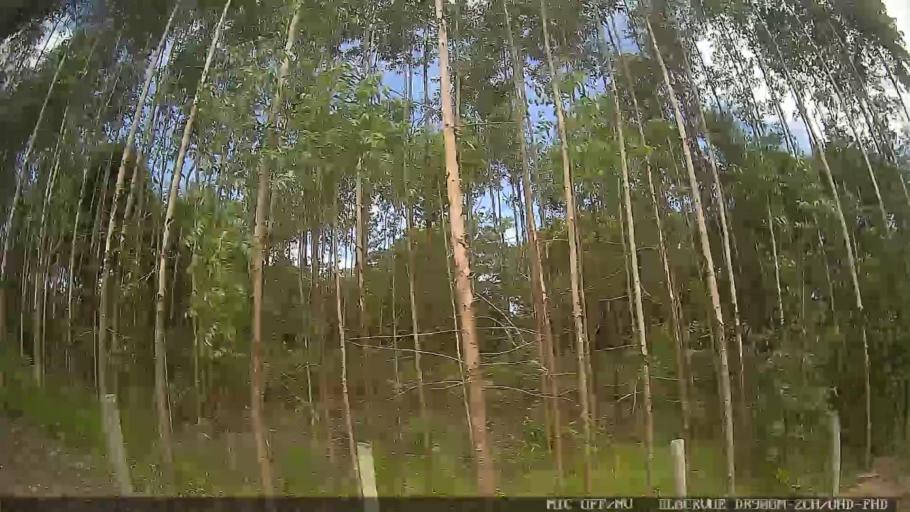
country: BR
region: Sao Paulo
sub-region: Conchas
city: Conchas
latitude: -22.9988
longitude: -47.9996
